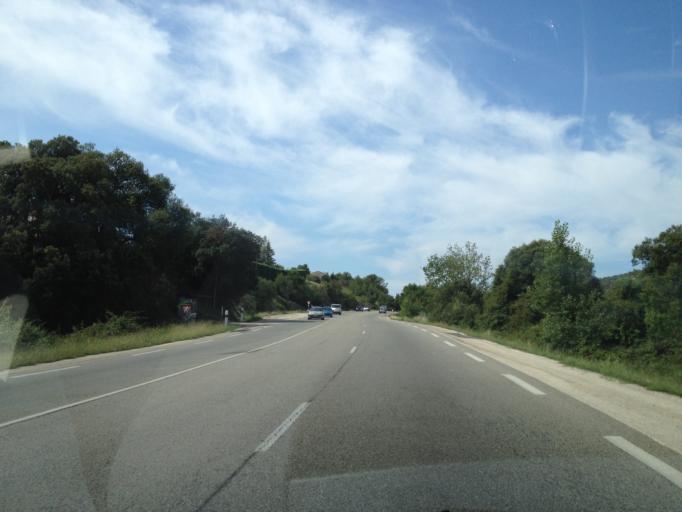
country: FR
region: Languedoc-Roussillon
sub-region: Departement du Gard
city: Rousson
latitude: 44.2125
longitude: 4.1481
